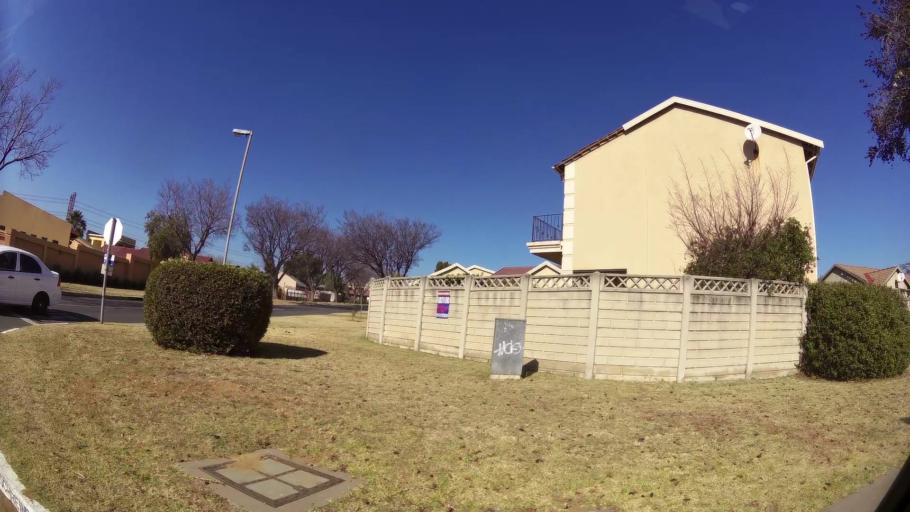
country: ZA
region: Gauteng
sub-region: City of Johannesburg Metropolitan Municipality
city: Johannesburg
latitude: -26.2395
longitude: 28.1042
